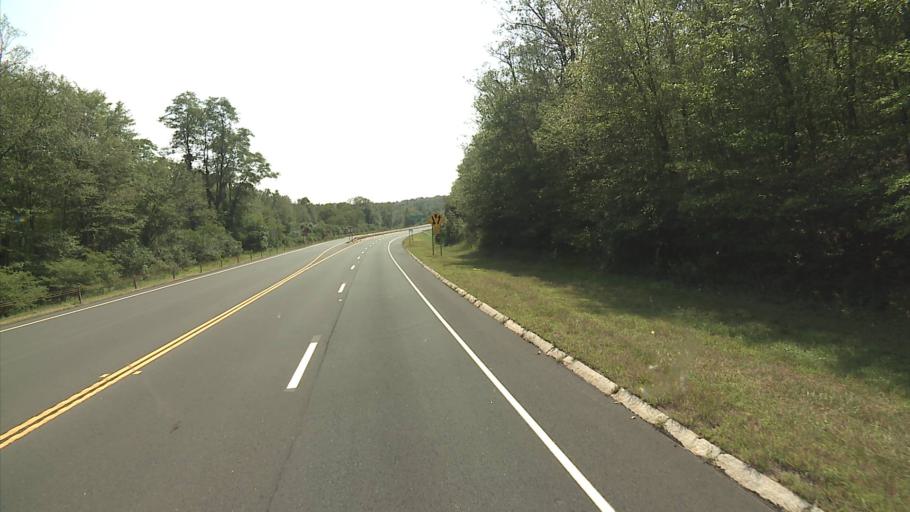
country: US
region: Connecticut
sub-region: Middlesex County
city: East Haddam
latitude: 41.4242
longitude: -72.4907
